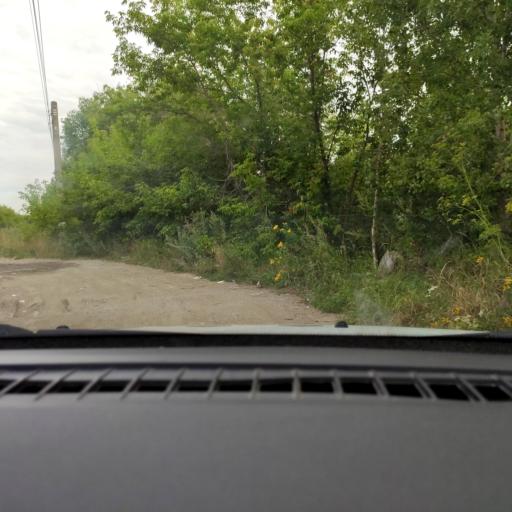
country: RU
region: Perm
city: Gamovo
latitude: 57.9006
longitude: 56.1775
